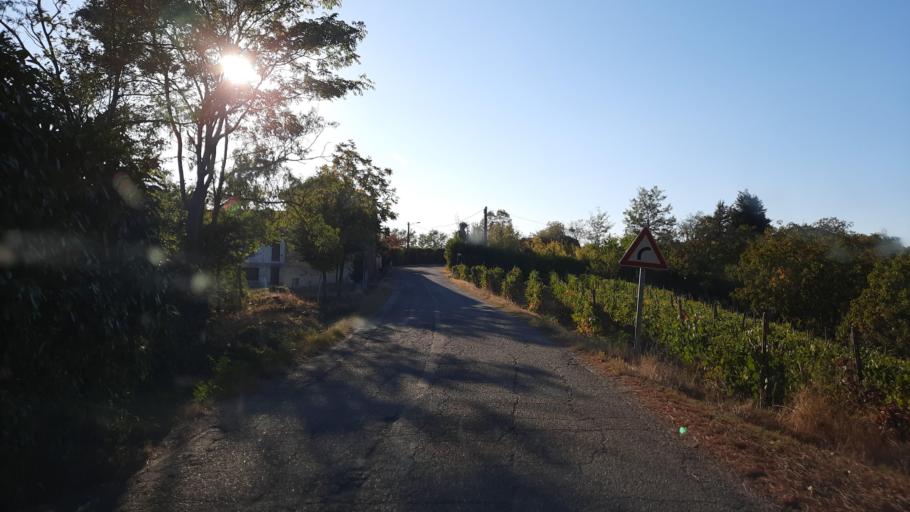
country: IT
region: Piedmont
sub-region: Provincia di Alessandria
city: Vignale Monferrato
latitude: 45.0036
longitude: 8.4140
